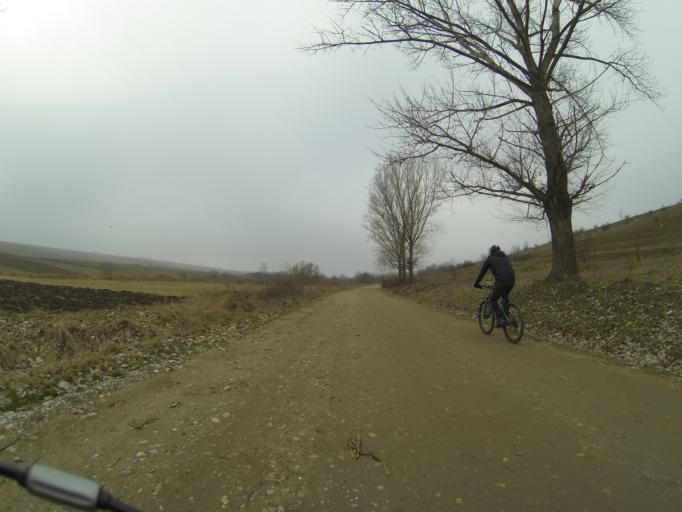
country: RO
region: Mehedinti
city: Padina Mica
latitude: 44.4882
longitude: 23.0157
